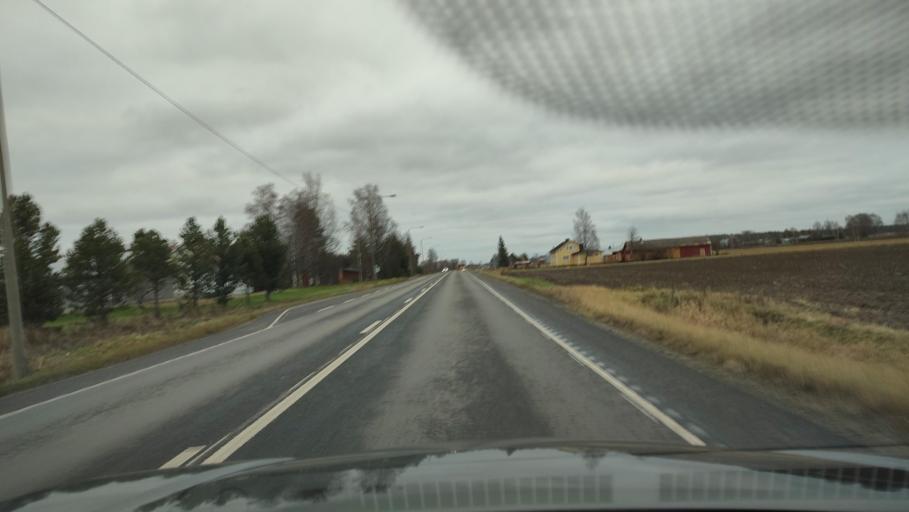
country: FI
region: Southern Ostrobothnia
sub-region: Seinaejoki
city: Ilmajoki
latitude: 62.7021
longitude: 22.5178
